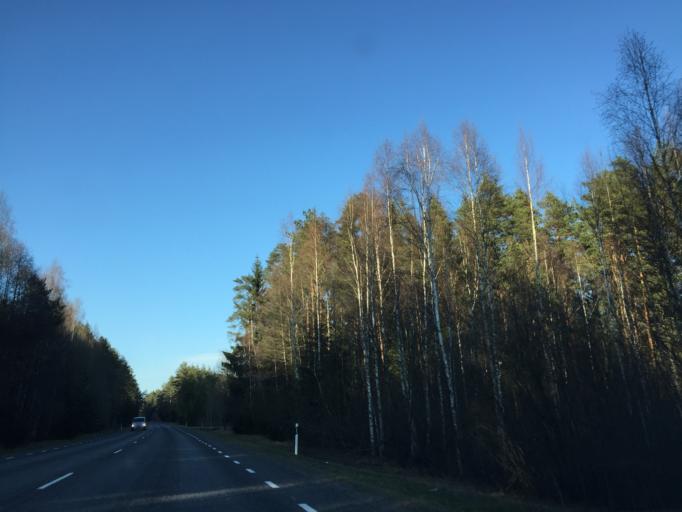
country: EE
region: Valgamaa
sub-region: Torva linn
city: Torva
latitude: 58.0977
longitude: 26.1085
